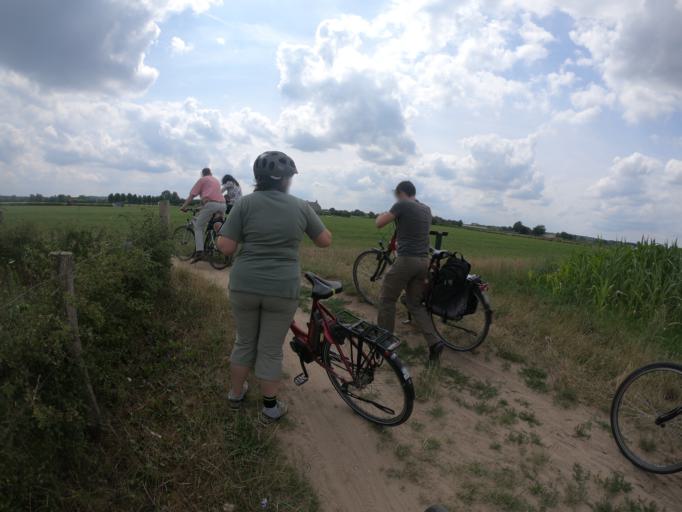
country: NL
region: Gelderland
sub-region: Gemeente Groesbeek
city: De Horst
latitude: 51.7880
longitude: 5.9622
